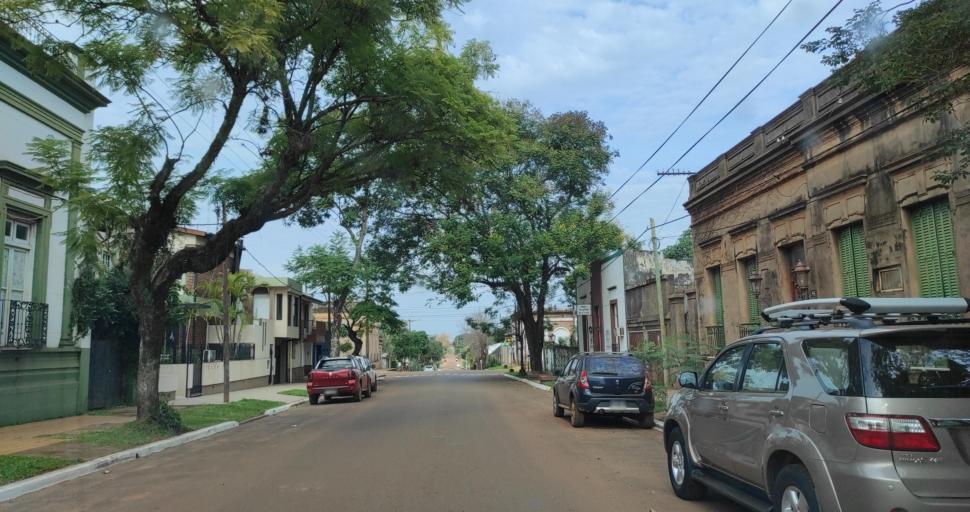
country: AR
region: Corrientes
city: Santo Tome
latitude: -28.5508
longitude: -56.0362
